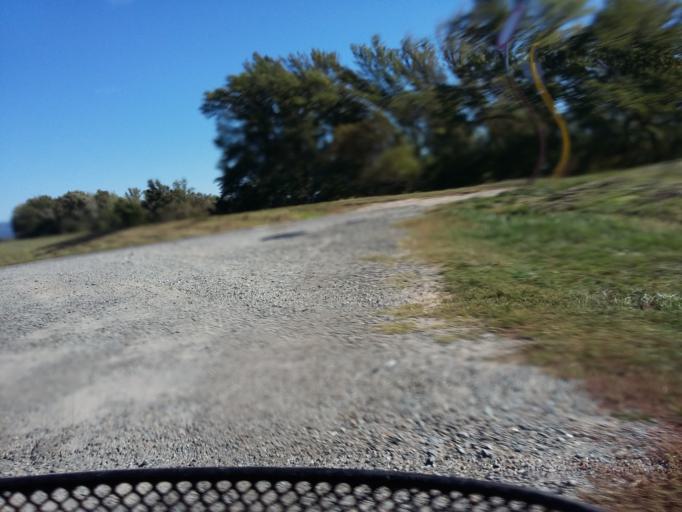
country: AT
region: Lower Austria
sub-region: Politischer Bezirk Ganserndorf
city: Marchegg
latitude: 48.2978
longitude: 16.9261
